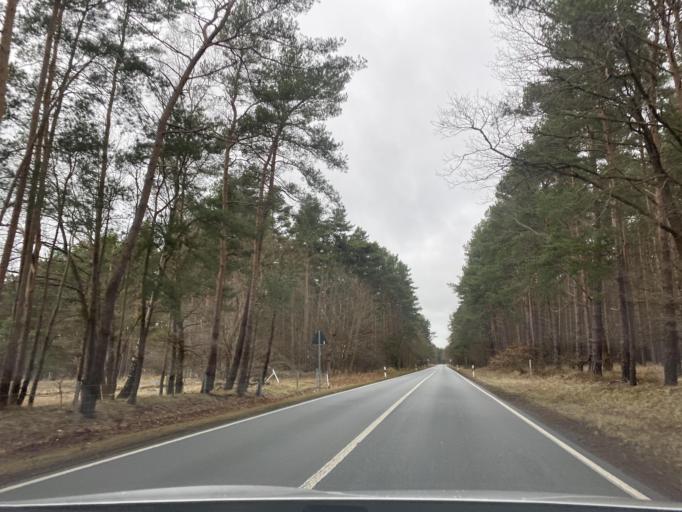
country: DE
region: Saxony
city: Rothenburg
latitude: 51.3898
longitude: 14.9527
